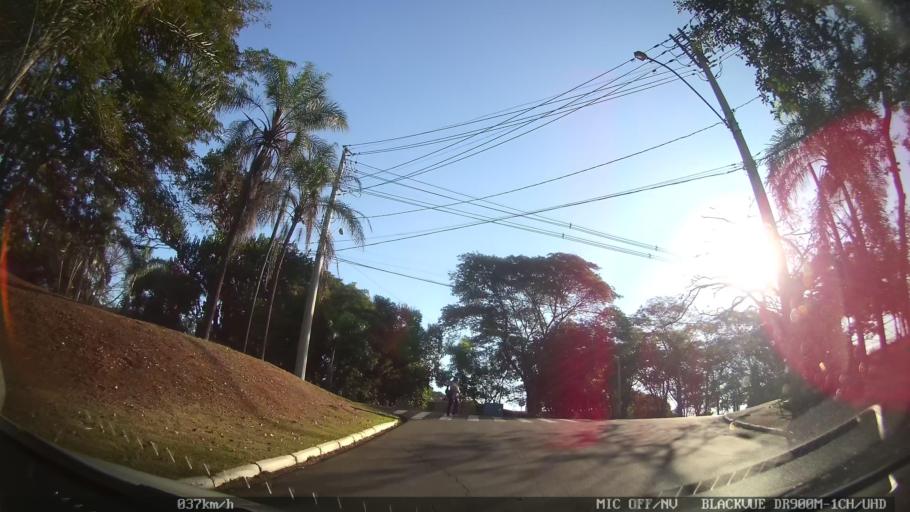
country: BR
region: Sao Paulo
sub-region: Nova Odessa
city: Nova Odessa
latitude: -22.7733
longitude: -47.2924
